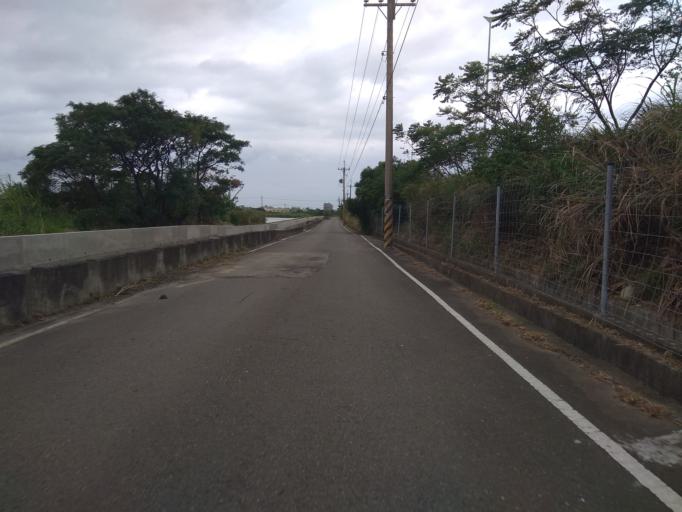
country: TW
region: Taiwan
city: Taoyuan City
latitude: 25.0452
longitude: 121.2190
